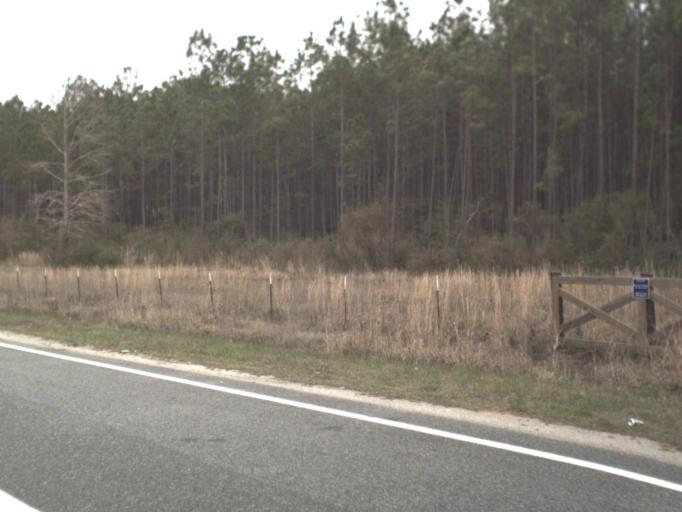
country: US
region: Florida
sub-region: Leon County
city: Woodville
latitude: 30.1986
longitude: -84.1628
